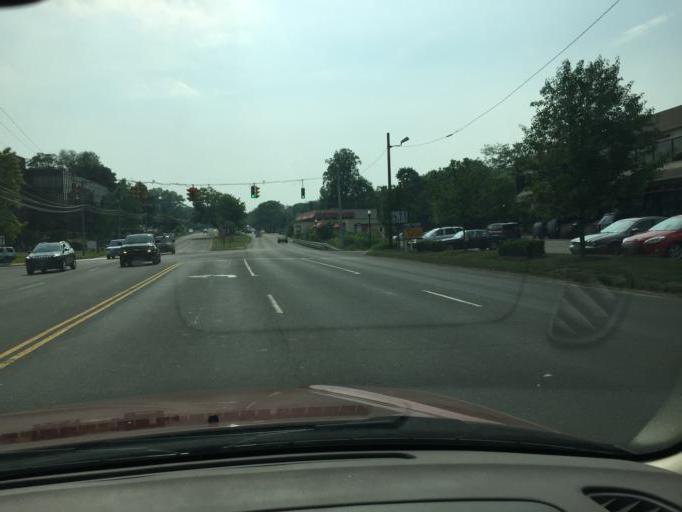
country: US
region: Connecticut
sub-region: Fairfield County
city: Westport
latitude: 41.1382
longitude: -73.3350
